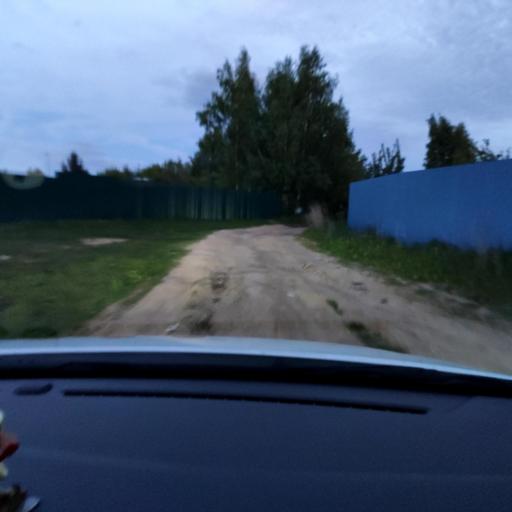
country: RU
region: Tatarstan
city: Stolbishchi
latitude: 55.5946
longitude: 49.0984
